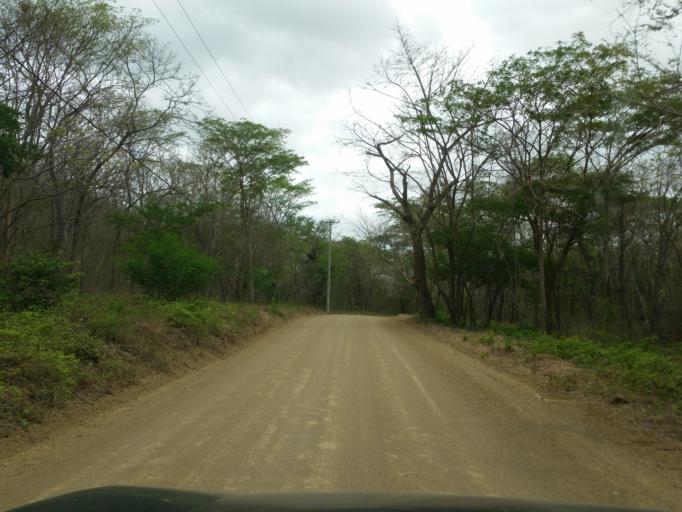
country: NI
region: Rivas
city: Tola
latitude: 11.4335
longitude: -86.0775
